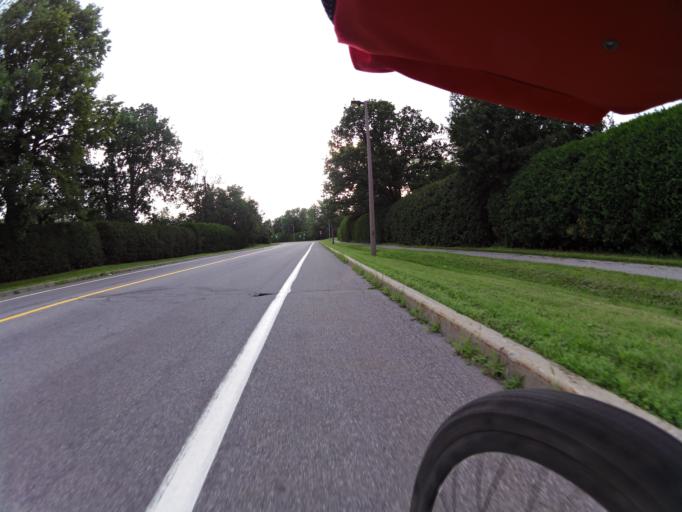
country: CA
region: Ontario
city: Bells Corners
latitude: 45.3273
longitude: -75.9075
